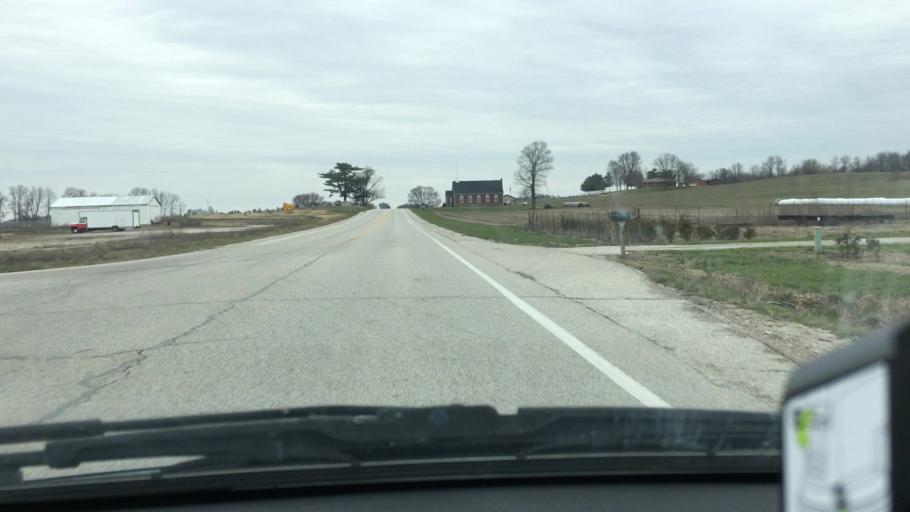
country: US
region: Indiana
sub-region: Greene County
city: Bloomfield
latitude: 38.9747
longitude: -87.0164
